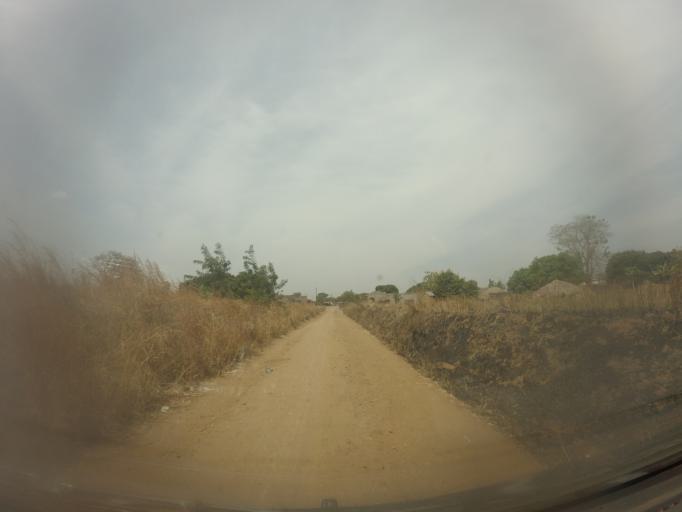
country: UG
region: Northern Region
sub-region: Arua District
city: Arua
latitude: 2.7724
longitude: 31.0365
